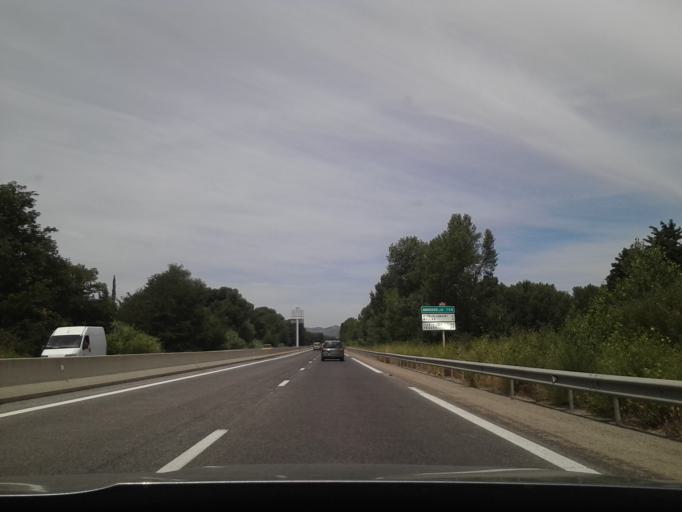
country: FR
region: Languedoc-Roussillon
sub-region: Departement des Pyrenees-Orientales
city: Corneilla-la-Riviere
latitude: 42.6841
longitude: 2.7446
